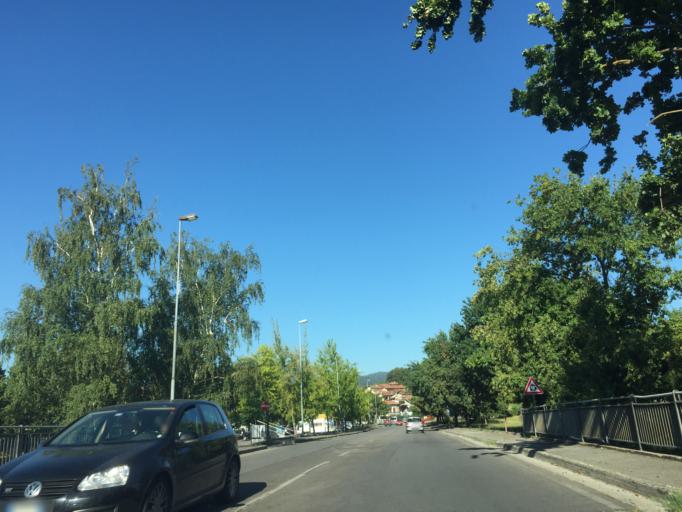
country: IT
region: Tuscany
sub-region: Provincia di Pistoia
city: Pistoia
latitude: 43.9441
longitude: 10.9138
